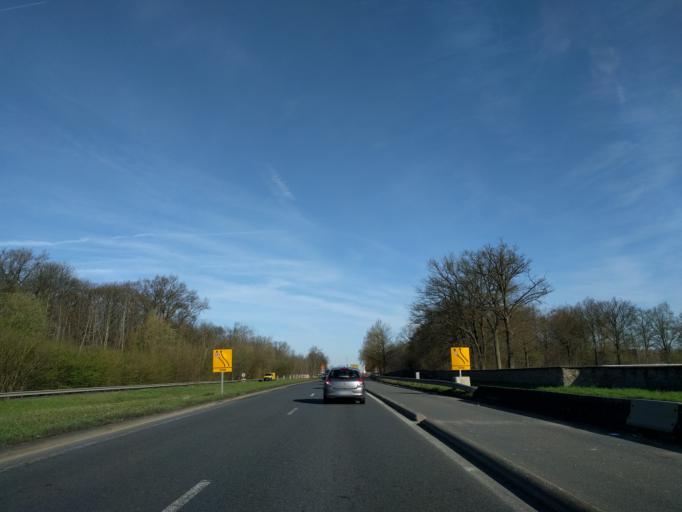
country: FR
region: Ile-de-France
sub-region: Departement du Val-de-Marne
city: Boissy-Saint-Leger
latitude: 48.7360
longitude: 2.5192
